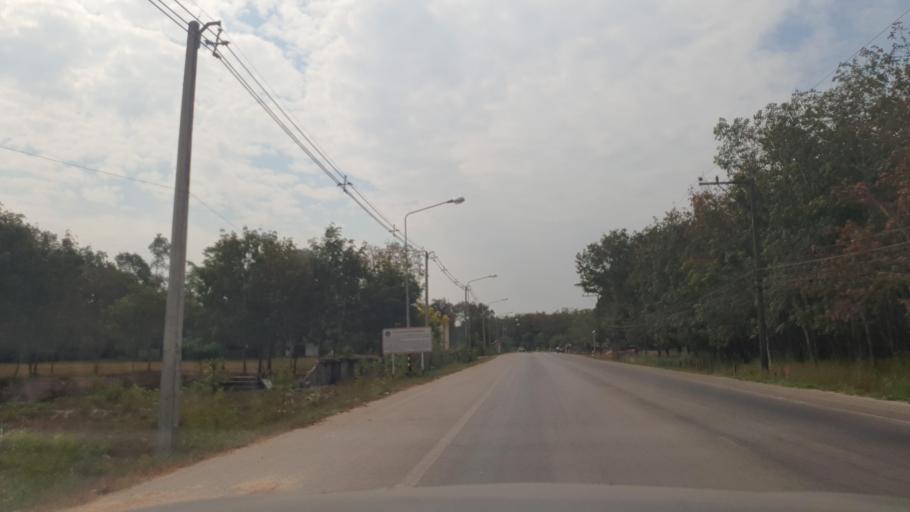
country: TH
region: Changwat Bueng Kan
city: Si Wilai
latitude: 18.3010
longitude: 103.8048
